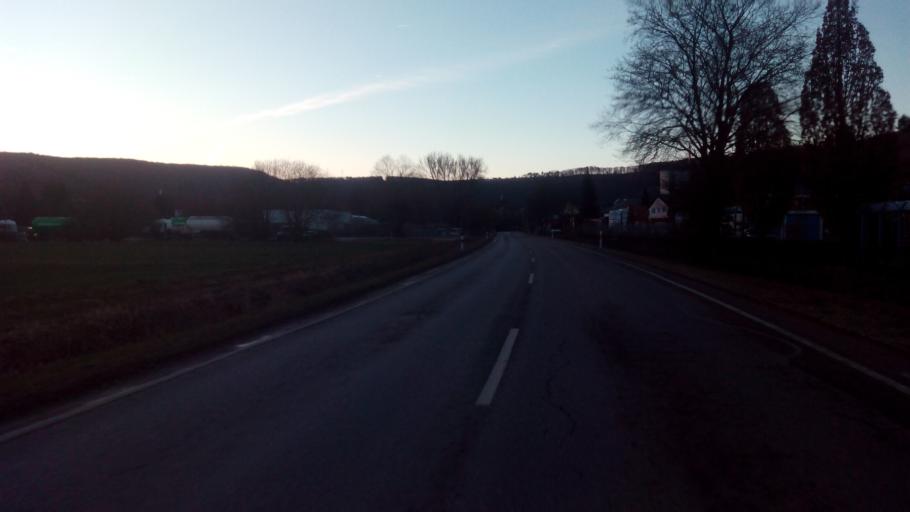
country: DE
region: Baden-Wuerttemberg
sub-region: Tuebingen Region
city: Schelklingen
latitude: 48.3698
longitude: 9.7415
